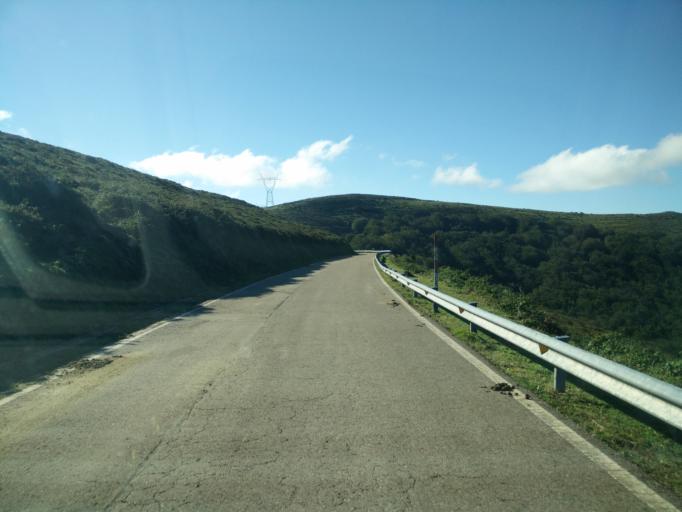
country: ES
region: Cantabria
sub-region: Provincia de Cantabria
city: San Pedro del Romeral
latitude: 43.0448
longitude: -3.8512
